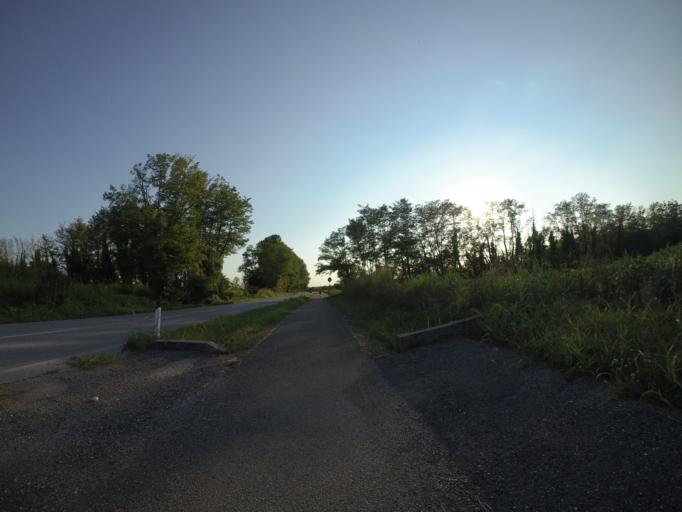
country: IT
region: Friuli Venezia Giulia
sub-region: Provincia di Udine
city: Bressa
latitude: 46.0375
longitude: 13.1676
